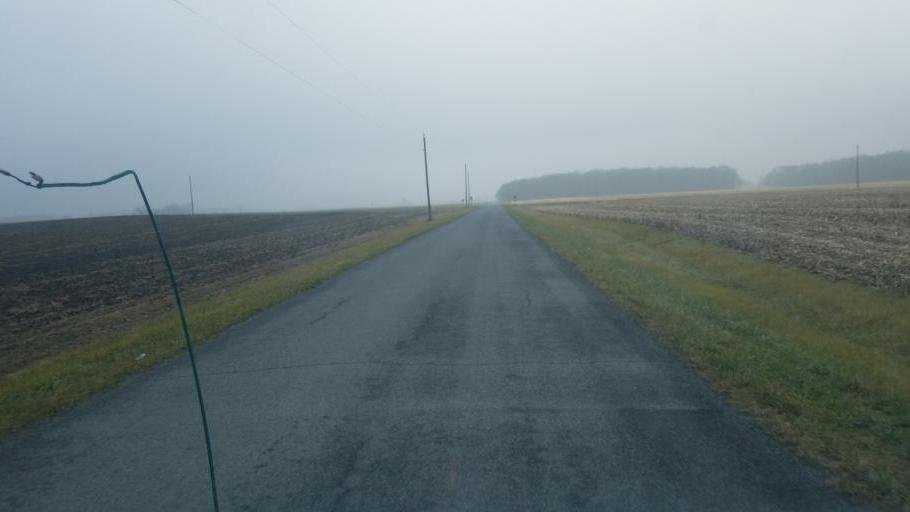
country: US
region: Ohio
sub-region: Hardin County
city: Kenton
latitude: 40.5004
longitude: -83.5379
